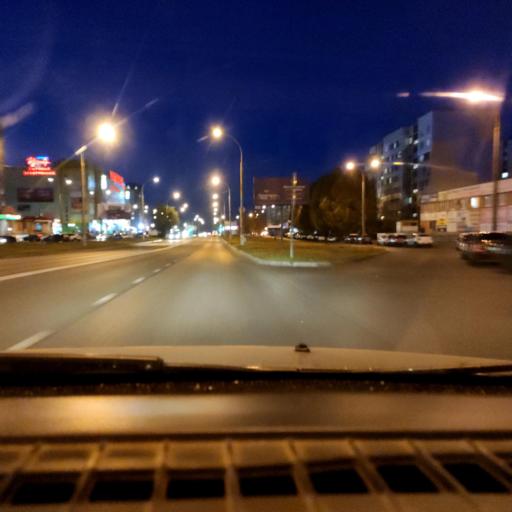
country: RU
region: Samara
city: Tol'yatti
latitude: 53.5419
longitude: 49.3605
